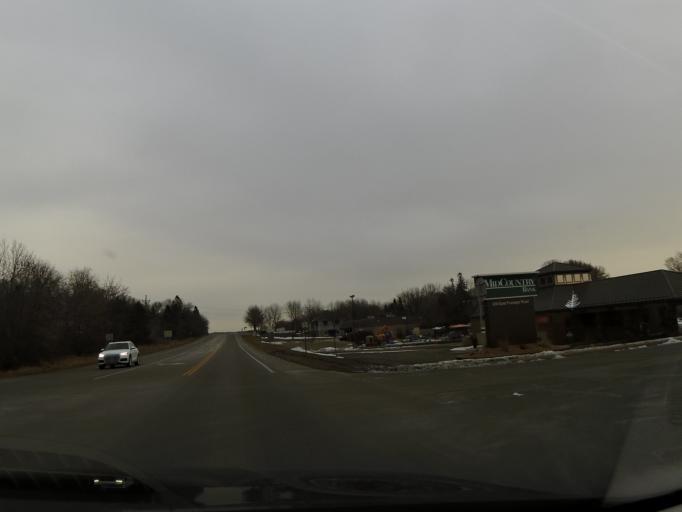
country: US
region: Minnesota
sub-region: Carver County
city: Waconia
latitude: 44.8443
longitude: -93.7835
